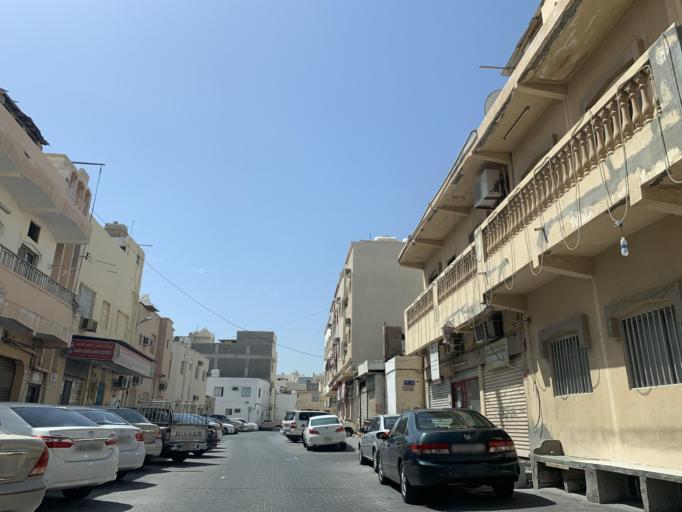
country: BH
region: Muharraq
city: Al Muharraq
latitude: 26.2600
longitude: 50.6108
